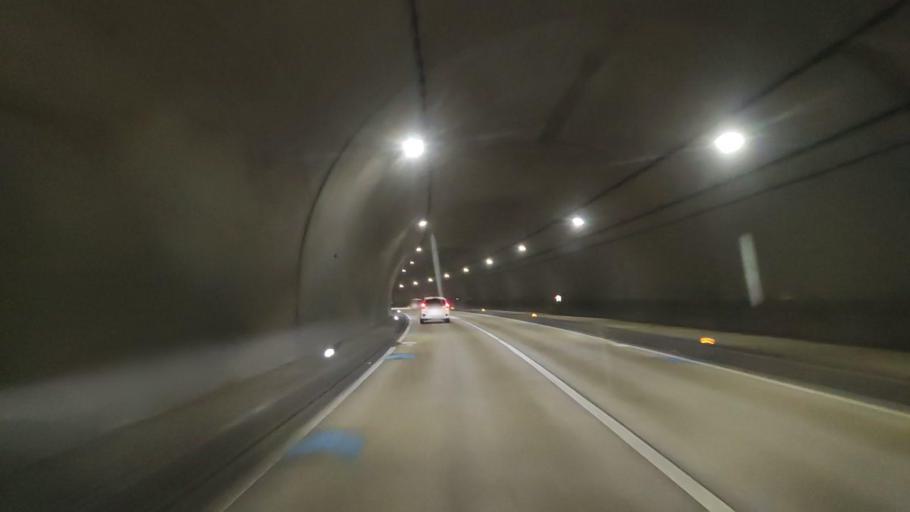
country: JP
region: Wakayama
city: Shingu
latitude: 33.7396
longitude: 135.9914
